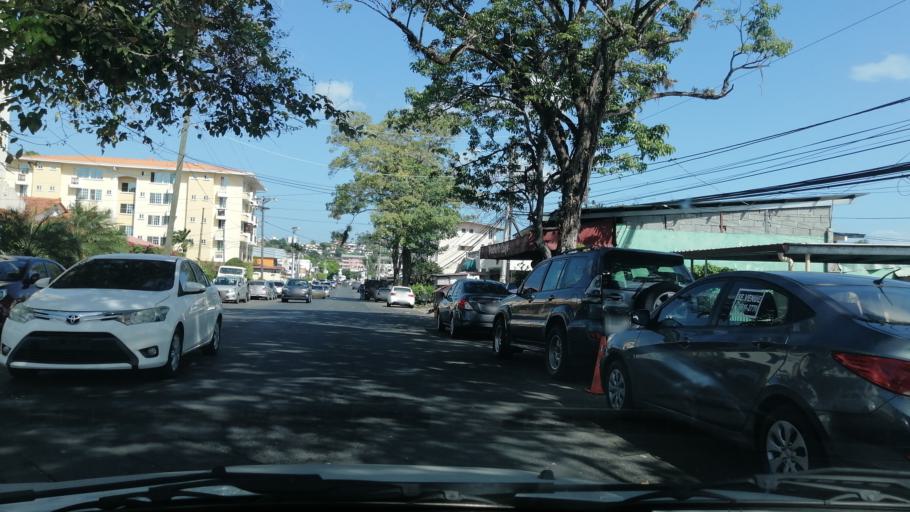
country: PA
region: Panama
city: Panama
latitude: 9.0064
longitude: -79.5229
